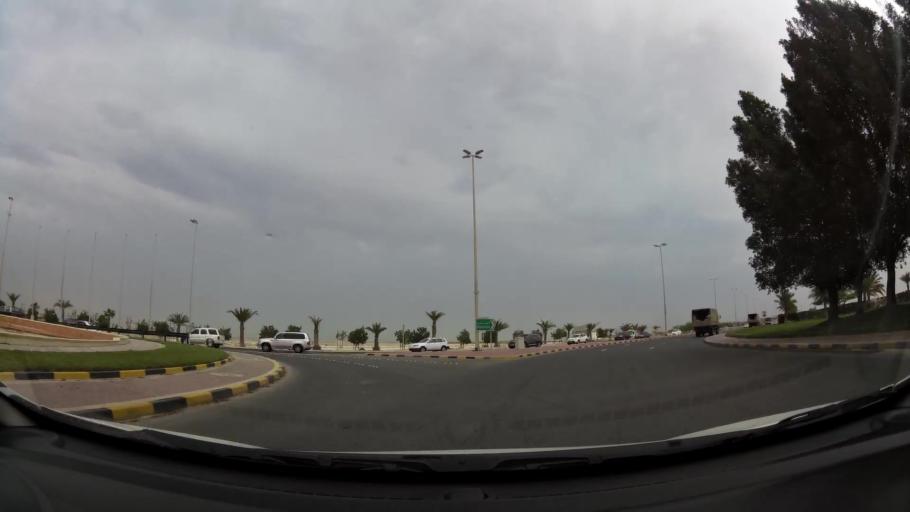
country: BH
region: Central Governorate
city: Dar Kulayb
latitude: 26.0725
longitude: 50.5277
